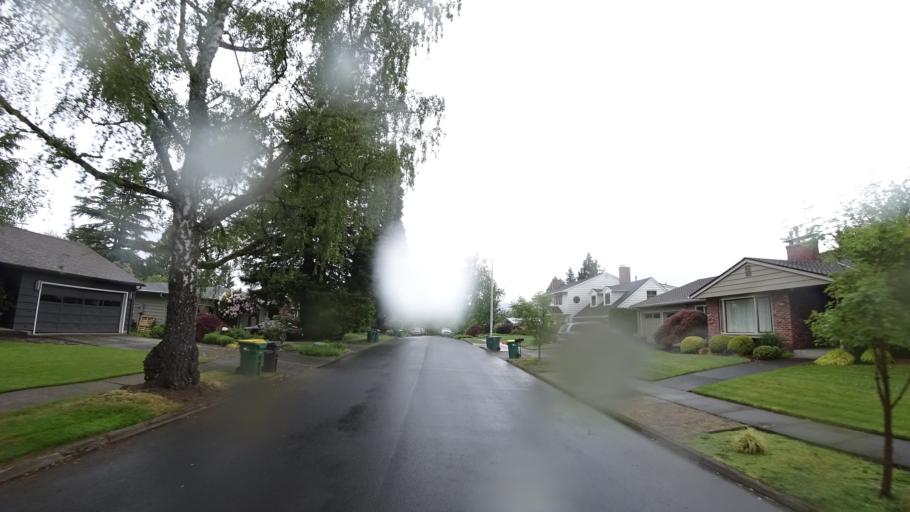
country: US
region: Oregon
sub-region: Washington County
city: Raleigh Hills
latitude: 45.4800
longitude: -122.7723
